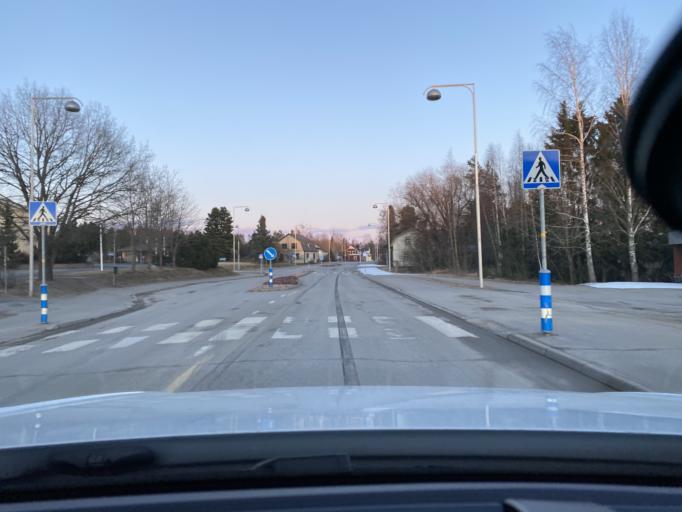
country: FI
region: Pirkanmaa
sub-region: Lounais-Pirkanmaa
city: Punkalaidun
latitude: 61.1097
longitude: 23.1198
